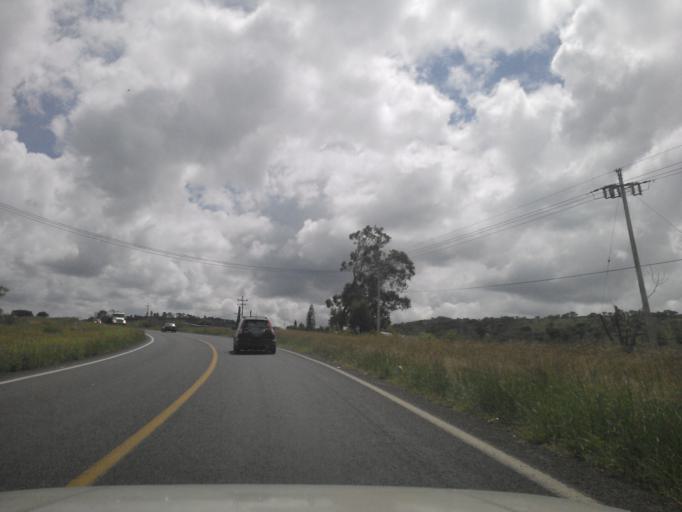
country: MX
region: Jalisco
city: Zapotlanejo
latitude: 20.6020
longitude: -102.9748
